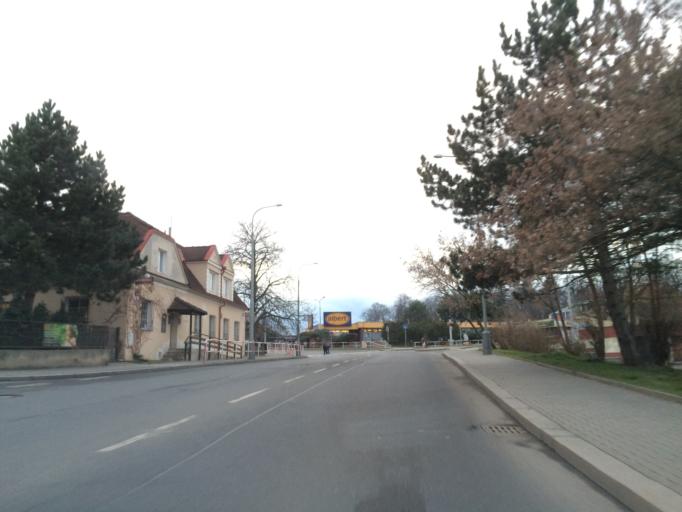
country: CZ
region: Praha
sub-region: Praha 1
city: Mala Strana
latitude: 50.1126
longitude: 14.3820
